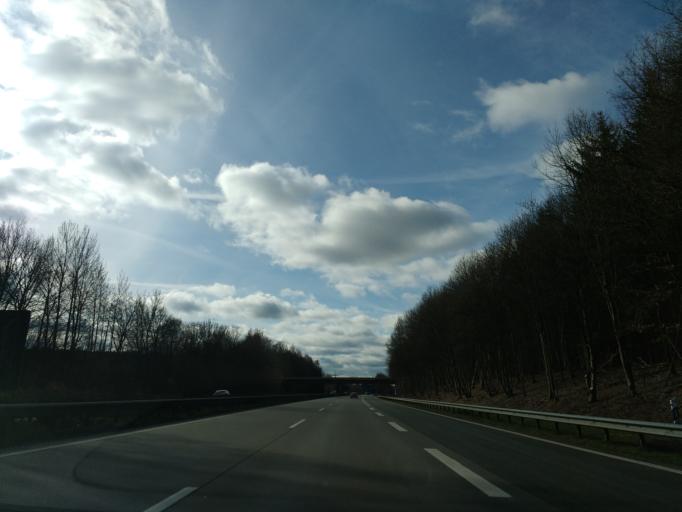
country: DE
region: Lower Saxony
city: Langen
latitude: 53.6127
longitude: 8.6614
